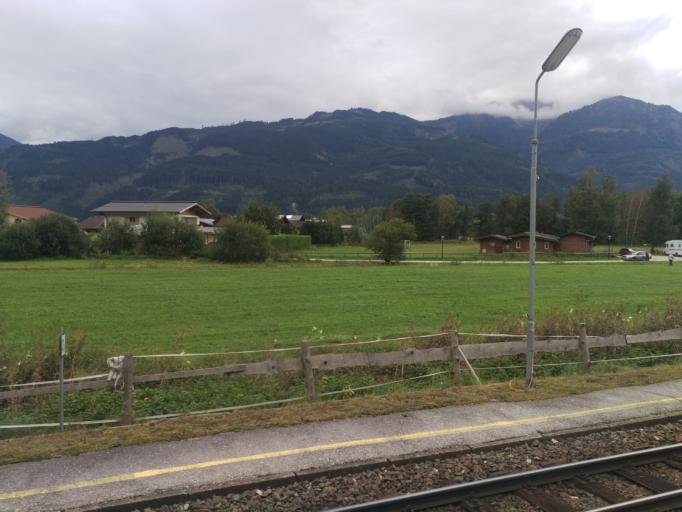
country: AT
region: Salzburg
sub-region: Politischer Bezirk Zell am See
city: Kaprun
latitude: 47.2948
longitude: 12.7764
